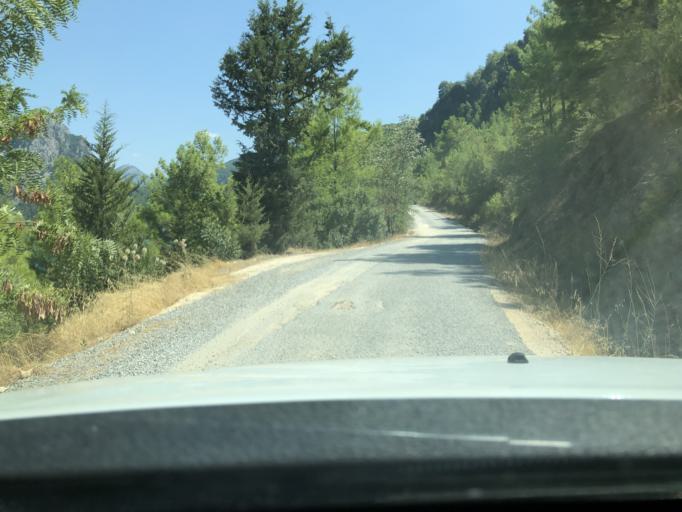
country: TR
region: Antalya
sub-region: Manavgat
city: Manavgat
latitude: 36.9101
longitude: 31.5507
